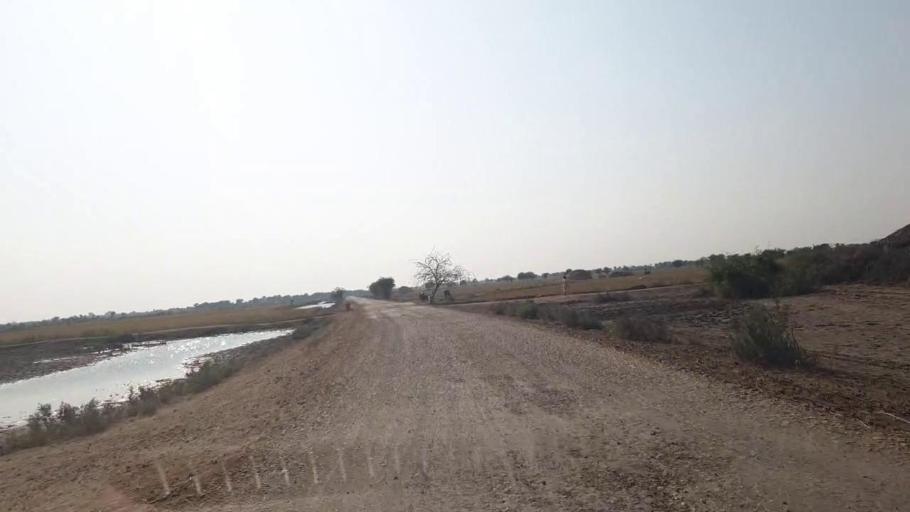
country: PK
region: Sindh
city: Matli
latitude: 24.9325
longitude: 68.6654
